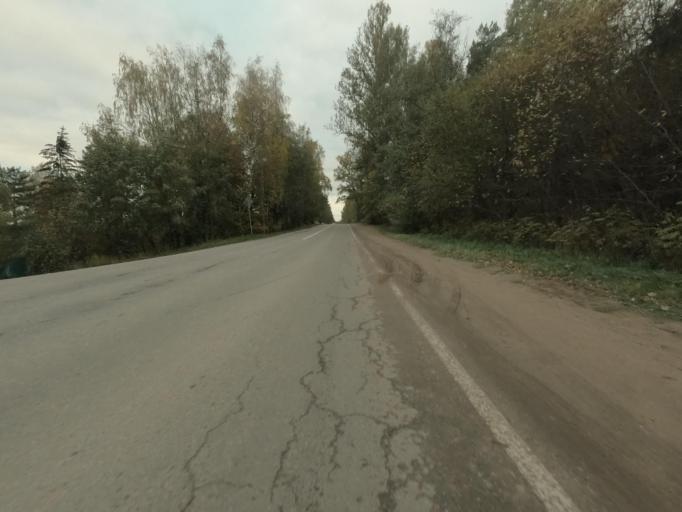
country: RU
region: Leningrad
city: Pavlovo
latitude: 59.7795
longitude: 30.9720
